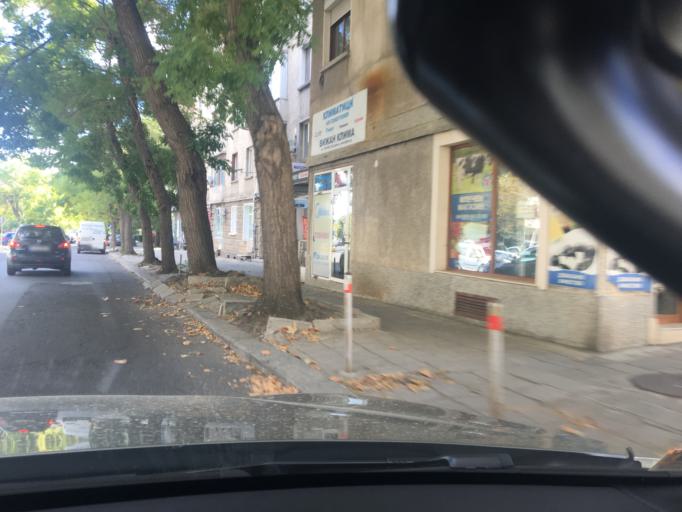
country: BG
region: Burgas
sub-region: Obshtina Burgas
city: Burgas
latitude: 42.5024
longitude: 27.4704
